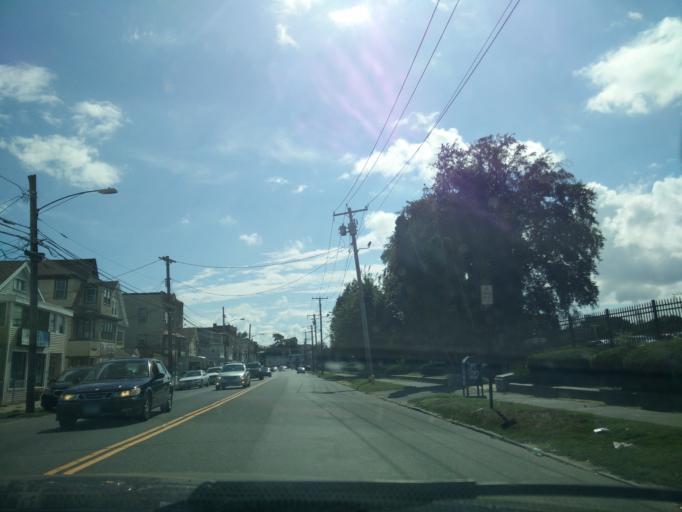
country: US
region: Connecticut
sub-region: Fairfield County
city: Bridgeport
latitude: 41.1903
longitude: -73.1987
